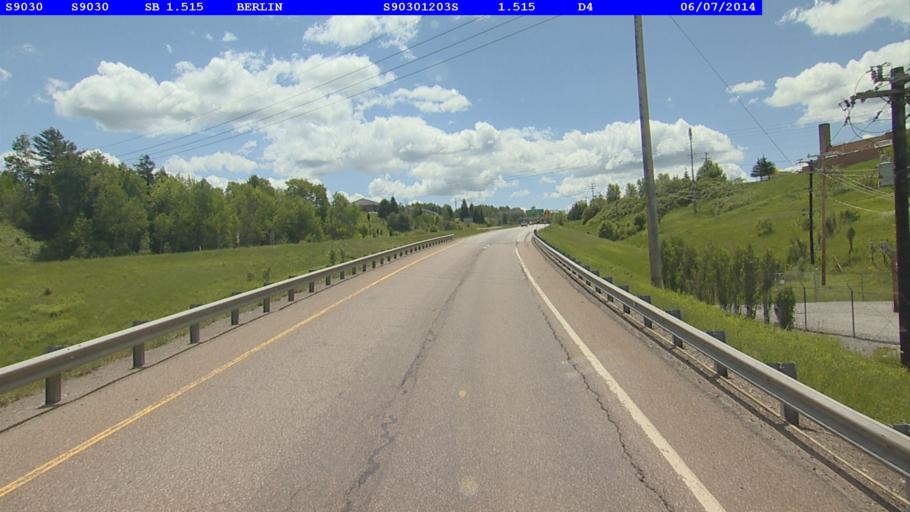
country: US
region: Vermont
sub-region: Washington County
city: Montpelier
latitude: 44.2218
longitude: -72.5581
